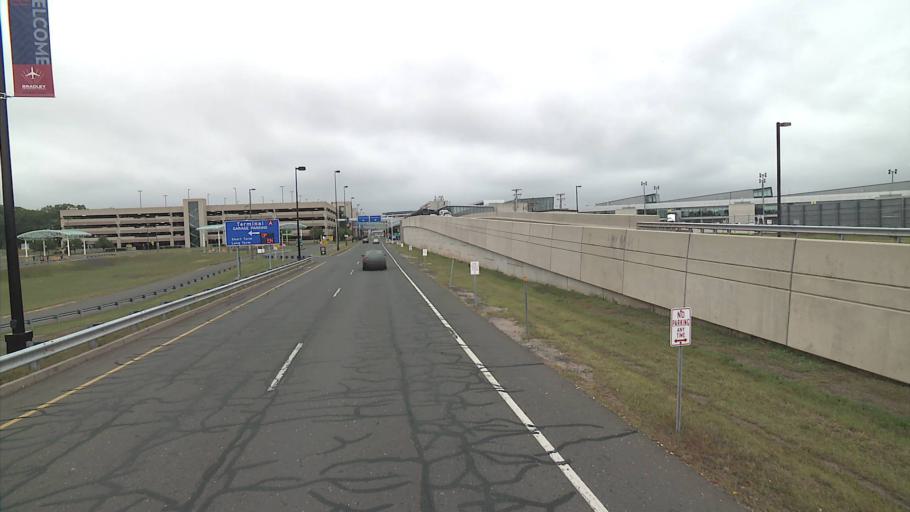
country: US
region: Connecticut
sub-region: Hartford County
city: Windsor Locks
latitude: 41.9278
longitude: -72.6828
